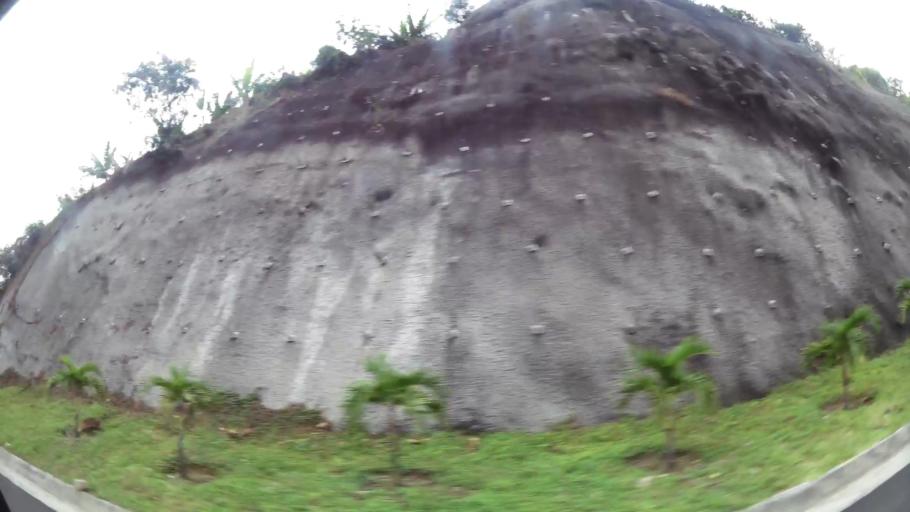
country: CO
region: Antioquia
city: Medellin
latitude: 6.2745
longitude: -75.6127
